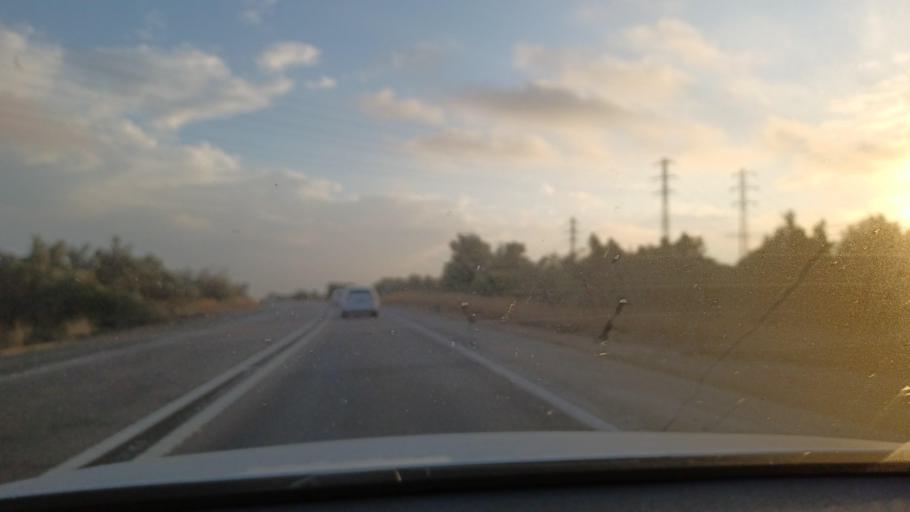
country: ES
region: Catalonia
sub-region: Provincia de Tarragona
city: Camarles
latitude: 40.7996
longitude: 0.6786
